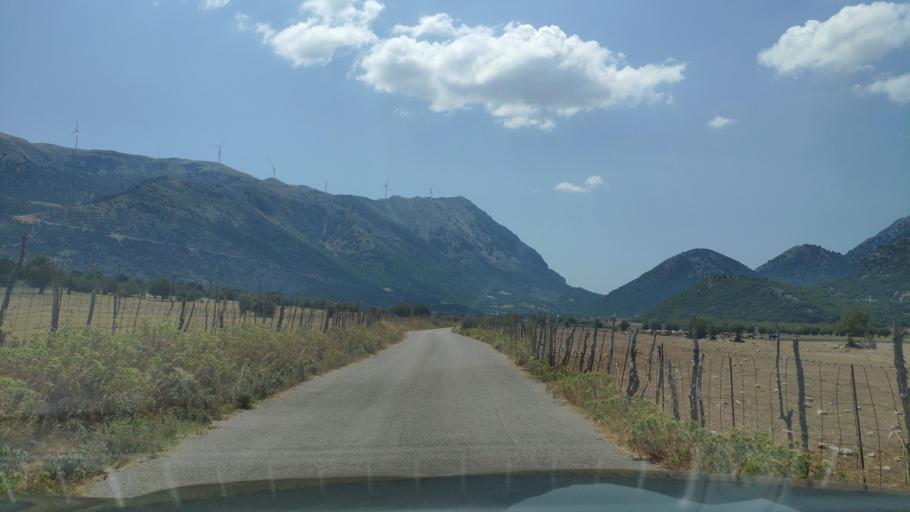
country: GR
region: West Greece
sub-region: Nomos Aitolias kai Akarnanias
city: Monastirakion
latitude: 38.7934
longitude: 20.9596
